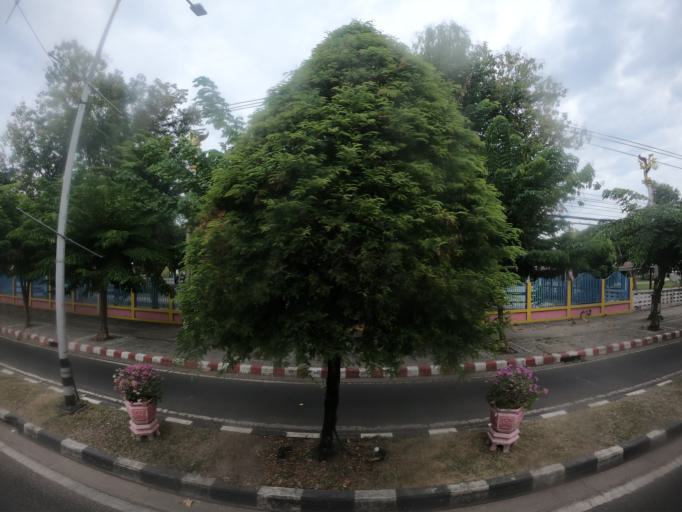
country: TH
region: Maha Sarakham
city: Maha Sarakham
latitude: 16.1872
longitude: 103.3001
